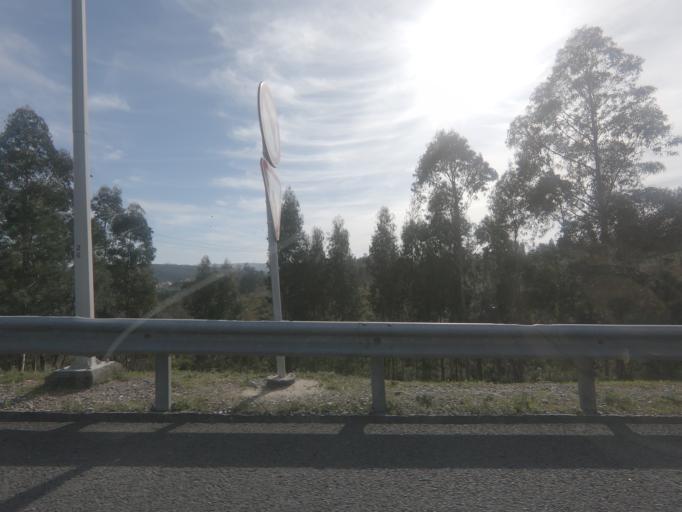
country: PT
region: Leiria
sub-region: Leiria
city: Caranguejeira
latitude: 39.7395
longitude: -8.7370
